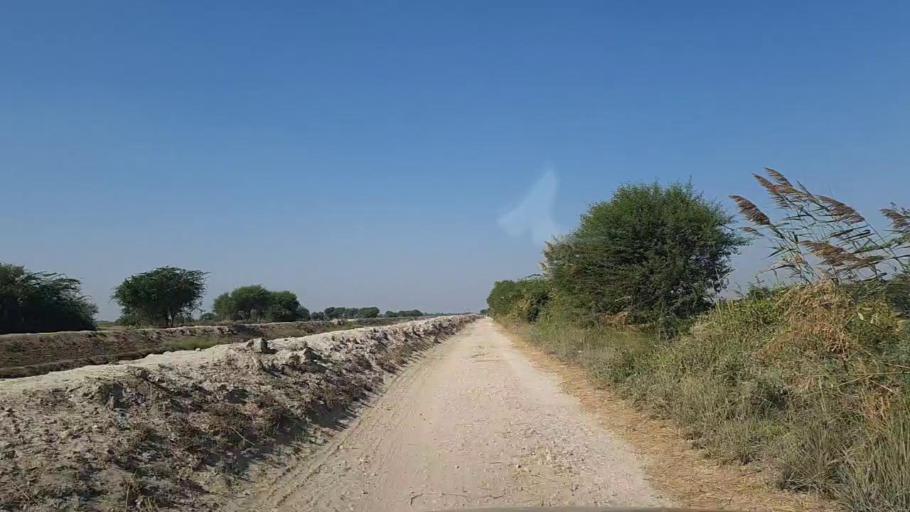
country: PK
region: Sindh
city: Mirpur Batoro
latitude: 24.7148
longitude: 68.2381
